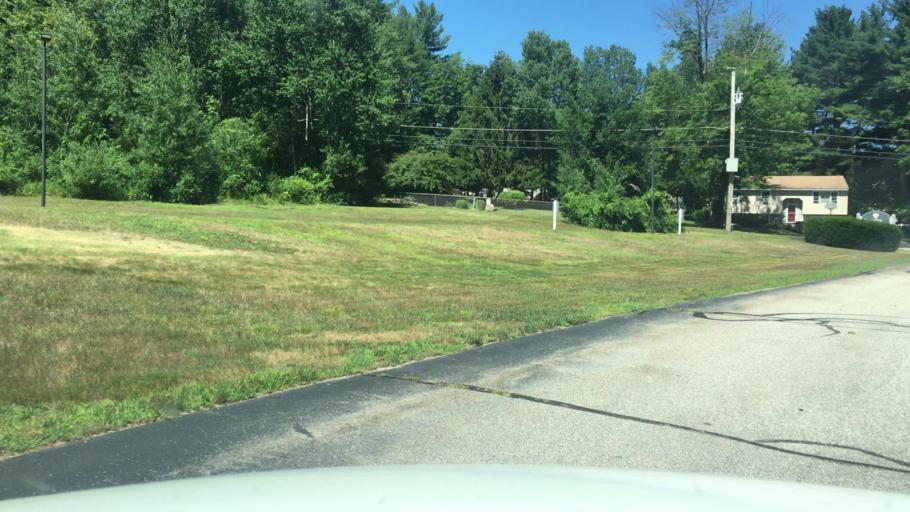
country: US
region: New Hampshire
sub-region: Merrimack County
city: Boscawen
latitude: 43.2739
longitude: -71.6038
